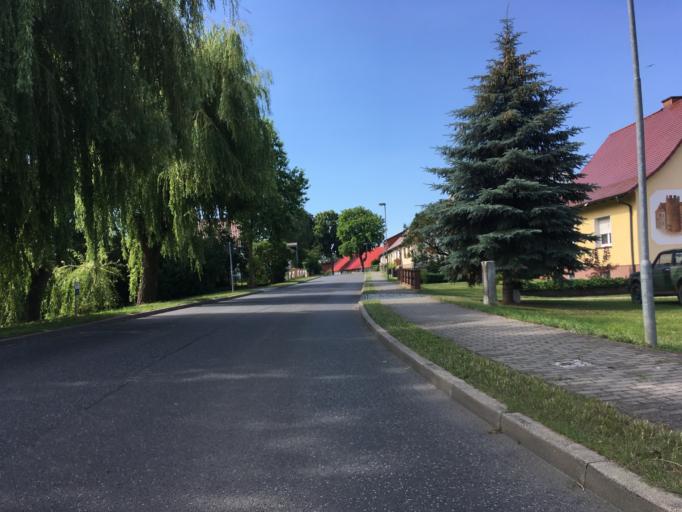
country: DE
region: Brandenburg
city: Zichow
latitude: 53.1925
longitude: 14.0397
